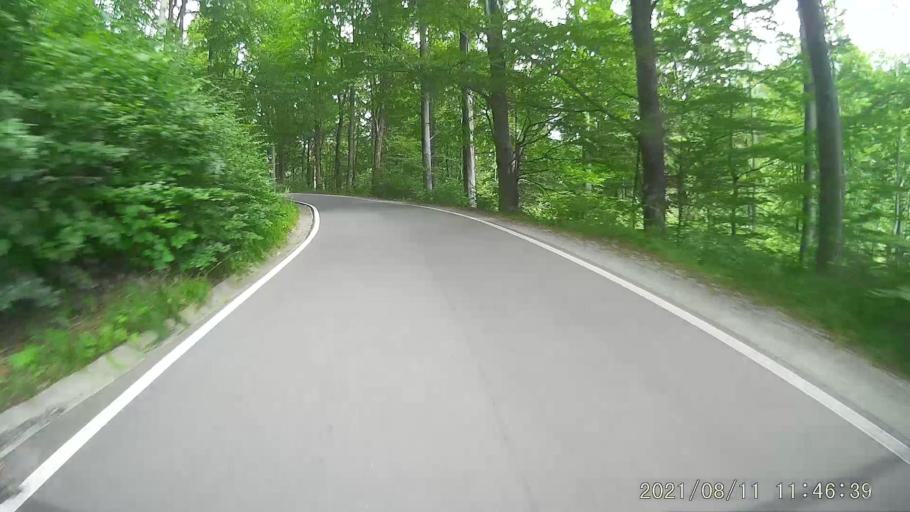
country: PL
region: Lower Silesian Voivodeship
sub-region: Powiat klodzki
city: Stronie Slaskie
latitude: 50.2447
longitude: 16.8504
